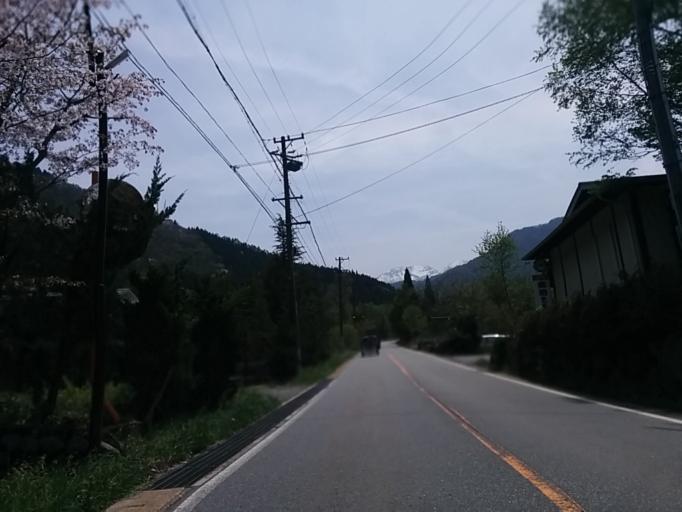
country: JP
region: Gifu
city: Takayama
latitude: 36.2329
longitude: 137.5334
